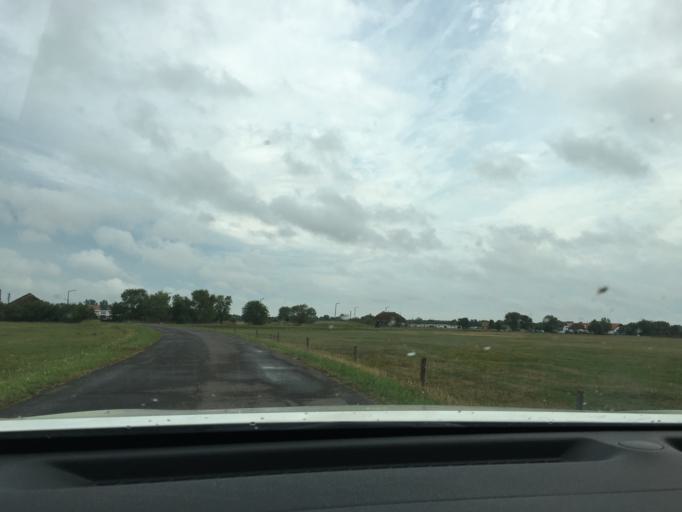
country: HU
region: Hajdu-Bihar
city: Hortobagy
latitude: 47.5768
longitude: 21.1449
